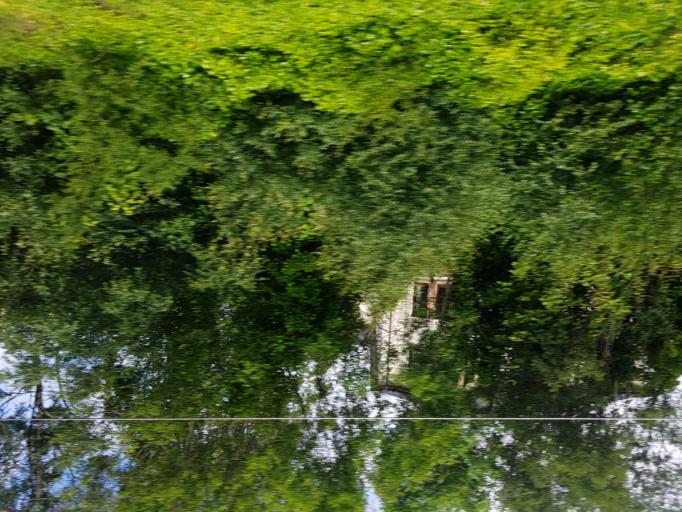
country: GB
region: Scotland
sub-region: East Dunbartonshire
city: Kirkintilloch
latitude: 55.9223
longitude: -4.1493
